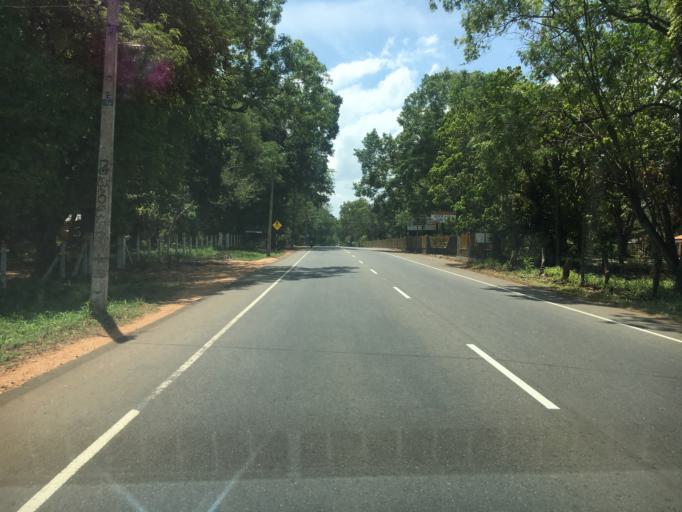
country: LK
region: North Central
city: Anuradhapura
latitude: 8.2686
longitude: 80.5034
